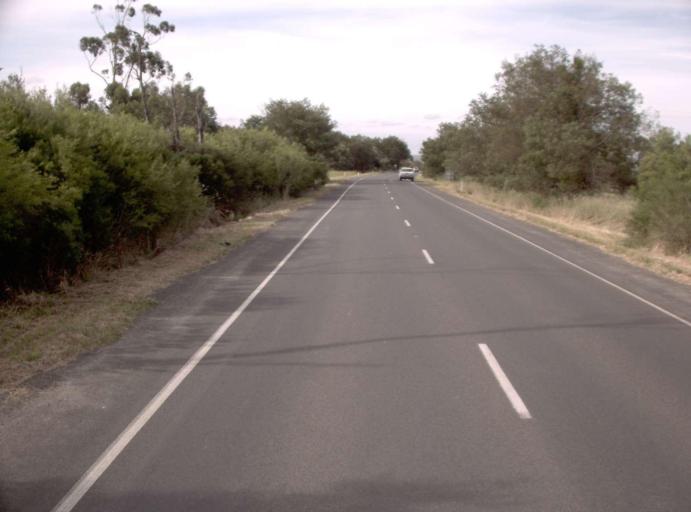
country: AU
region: Victoria
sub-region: Latrobe
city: Traralgon
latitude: -38.1560
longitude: 146.5535
